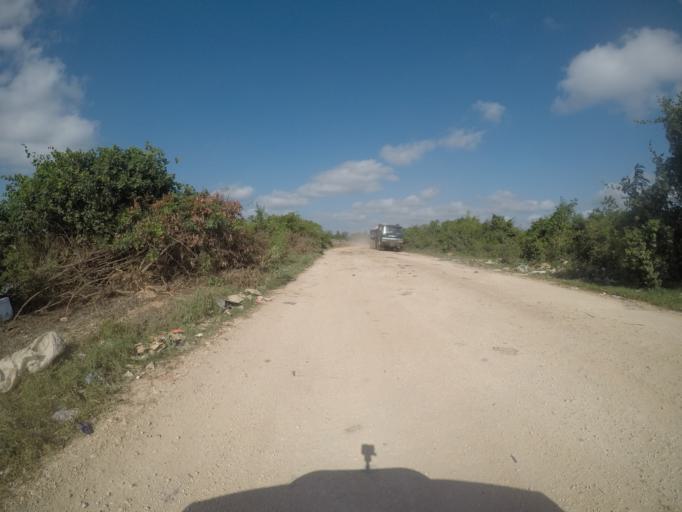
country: TZ
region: Zanzibar Central/South
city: Koani
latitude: -6.2187
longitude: 39.3284
